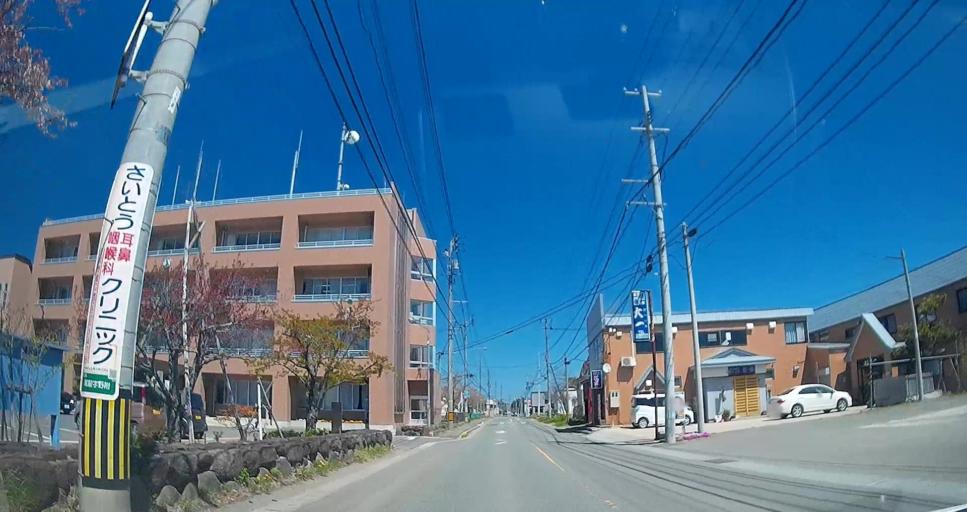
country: JP
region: Aomori
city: Misawa
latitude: 40.9670
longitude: 141.3749
